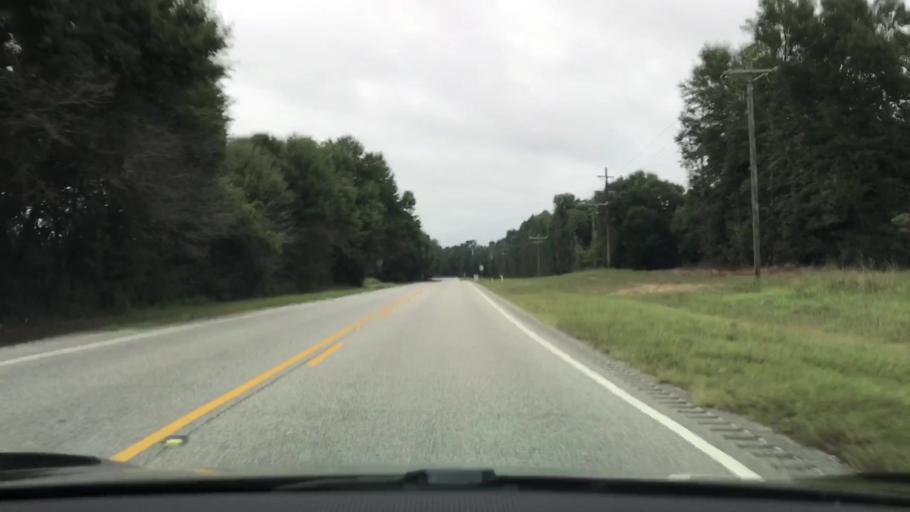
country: US
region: Alabama
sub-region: Coffee County
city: Elba
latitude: 31.3792
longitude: -86.0901
